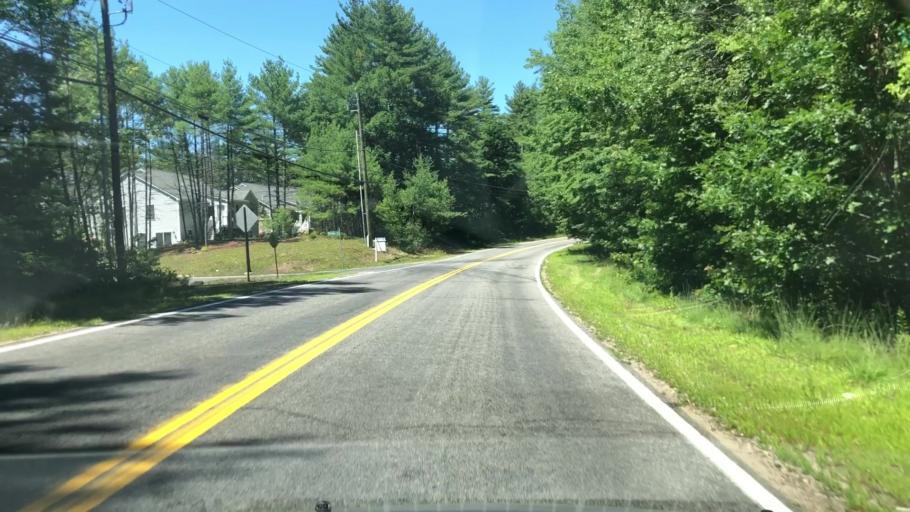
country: US
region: New Hampshire
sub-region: Hillsborough County
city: Milford
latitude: 42.8358
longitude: -71.6155
